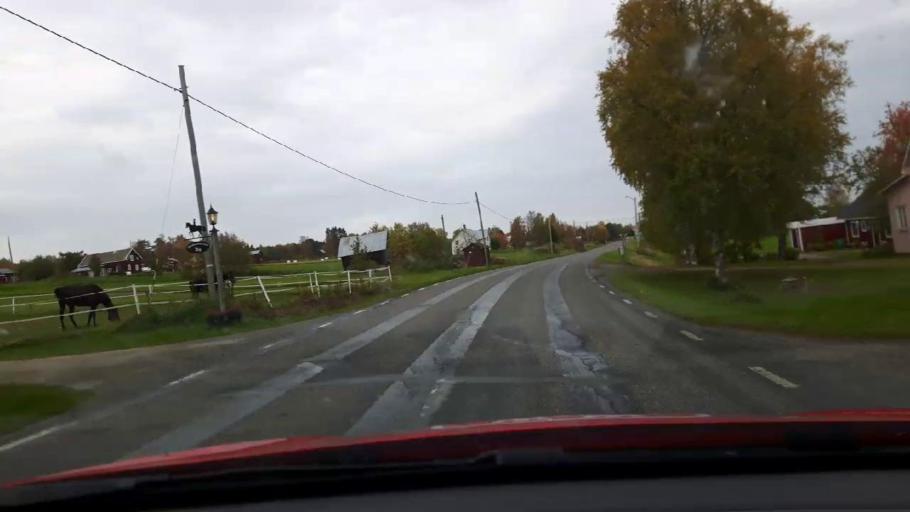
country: SE
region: Jaemtland
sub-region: Bergs Kommun
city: Hoverberg
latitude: 62.8330
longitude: 14.3859
